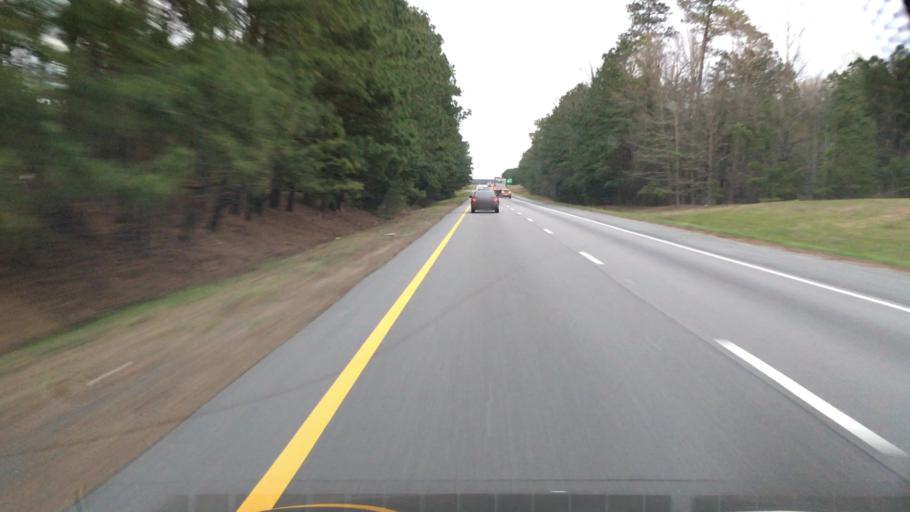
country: US
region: Virginia
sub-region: Sussex County
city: Sussex
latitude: 36.8468
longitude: -77.4334
